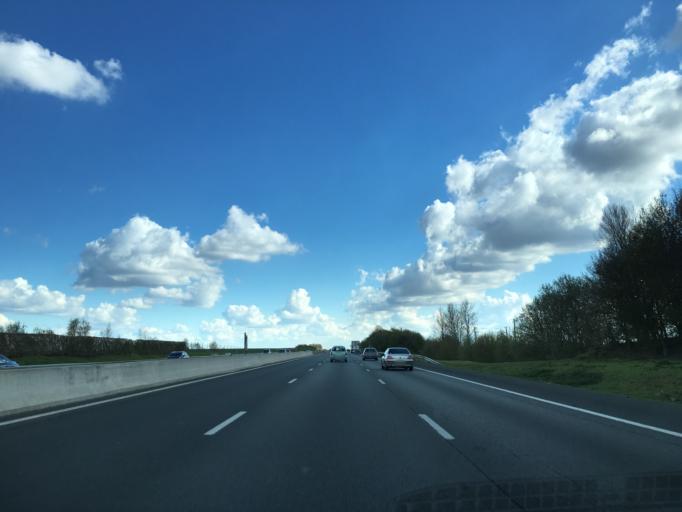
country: FR
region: Nord-Pas-de-Calais
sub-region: Departement du Pas-de-Calais
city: Croisilles
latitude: 50.2213
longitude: 2.8591
